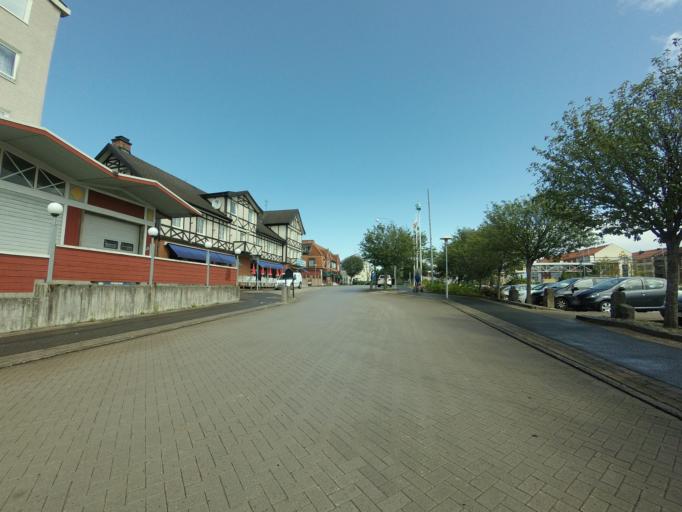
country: SE
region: Skane
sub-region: Osby Kommun
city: Osby
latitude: 56.3807
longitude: 13.9942
